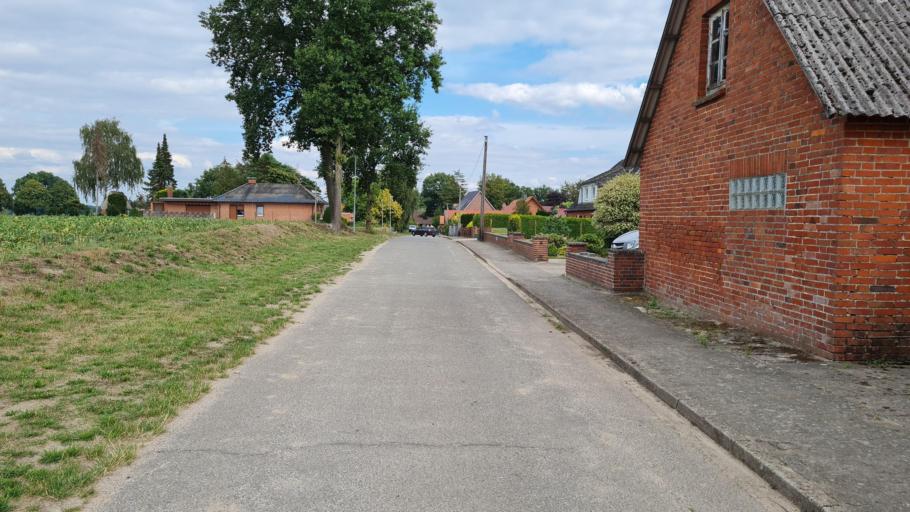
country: DE
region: Lower Saxony
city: Nahrendorf
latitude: 53.1584
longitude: 10.8030
